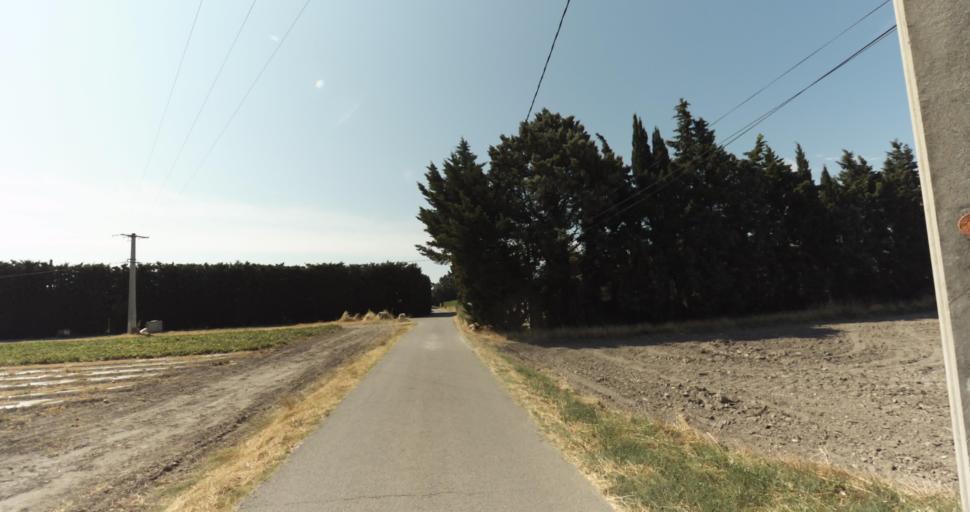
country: FR
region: Provence-Alpes-Cote d'Azur
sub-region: Departement du Vaucluse
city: Monteux
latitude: 44.0101
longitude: 4.9958
